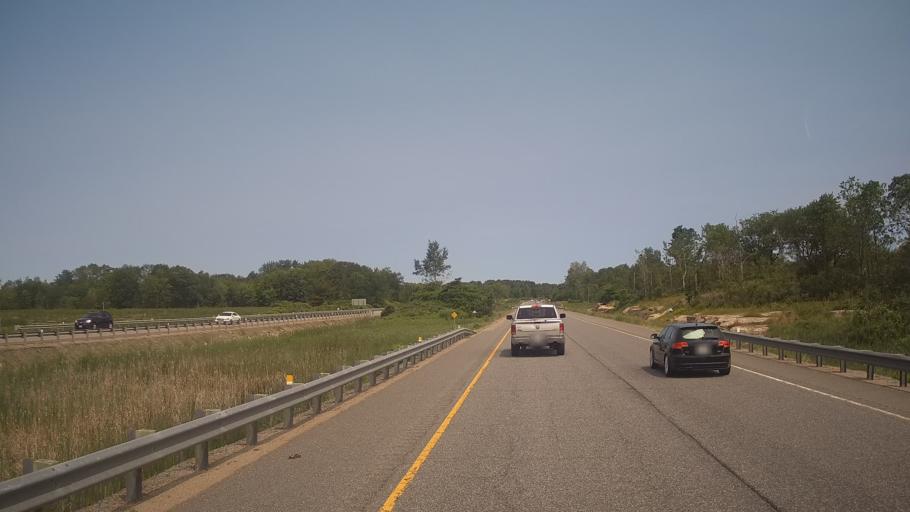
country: CA
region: Ontario
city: Midland
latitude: 44.8316
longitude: -79.7376
